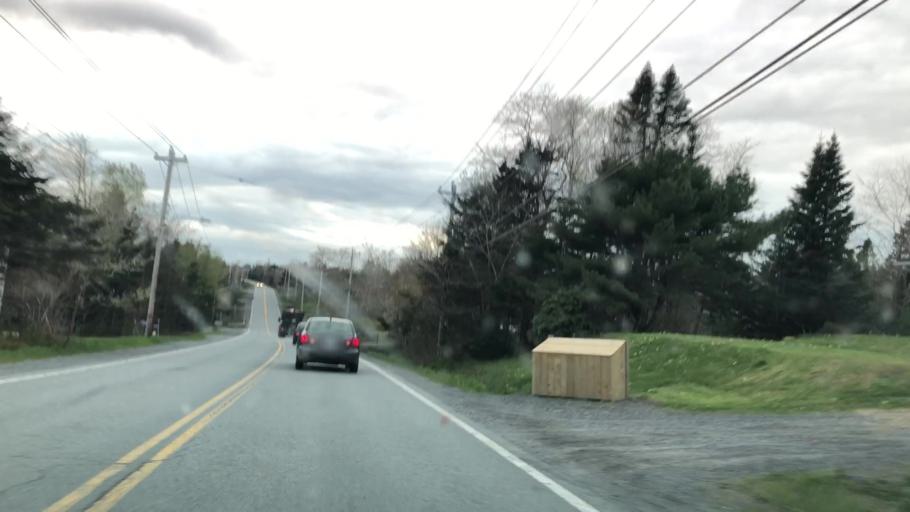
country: CA
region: Nova Scotia
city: Cole Harbour
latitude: 44.7839
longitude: -63.1627
